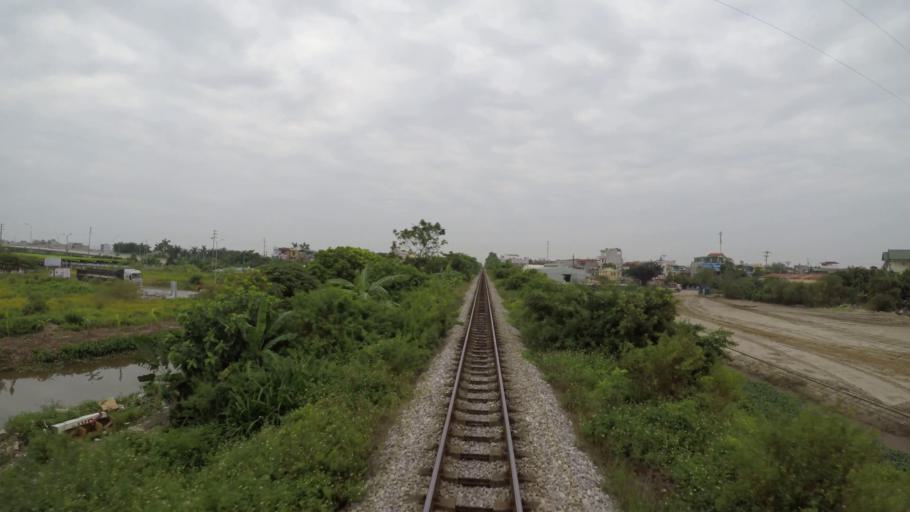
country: VN
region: Hai Duong
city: Thanh Pho Hai Duong
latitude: 20.9482
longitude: 106.3617
